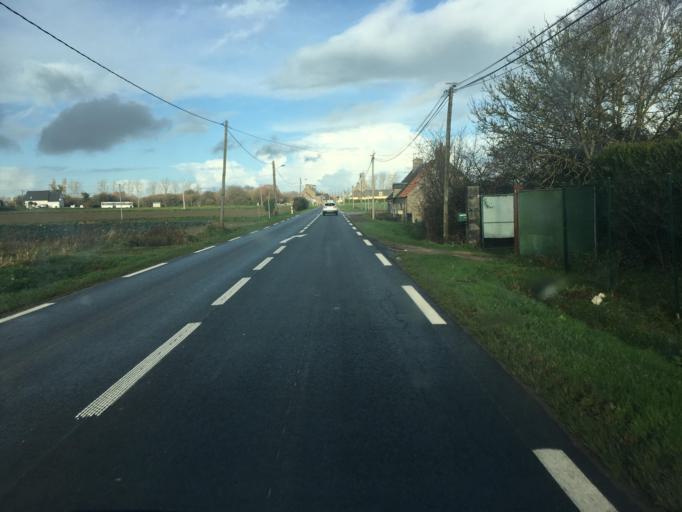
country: FR
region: Lower Normandy
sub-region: Departement de la Manche
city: Quettehou
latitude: 49.6181
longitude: -1.2918
